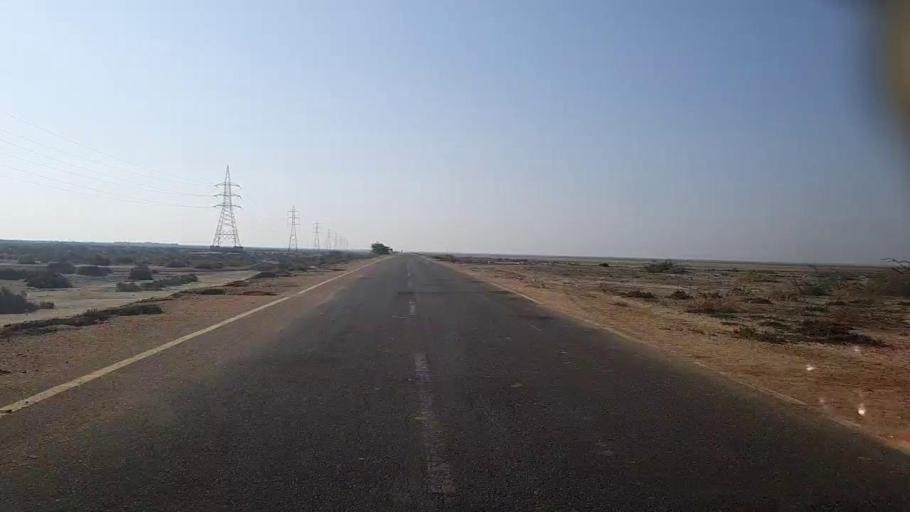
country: PK
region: Sindh
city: Mirpur Sakro
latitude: 24.6166
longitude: 67.4970
